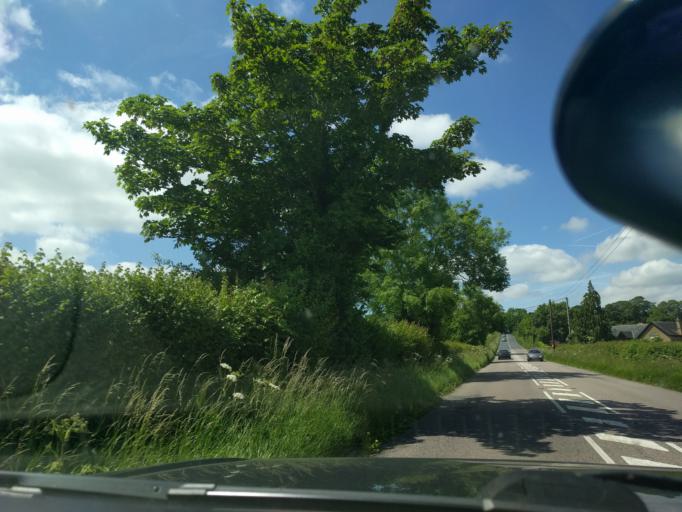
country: GB
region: England
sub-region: Wiltshire
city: Atworth
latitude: 51.3953
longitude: -2.2037
